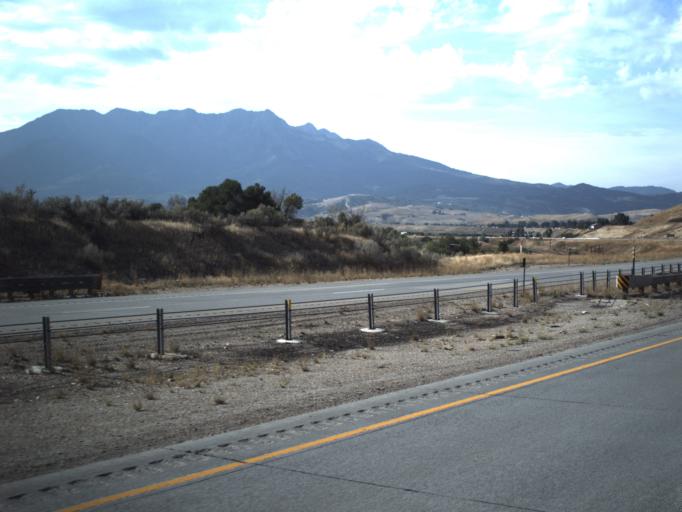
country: US
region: Utah
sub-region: Morgan County
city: Mountain Green
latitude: 41.1216
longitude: -111.7647
